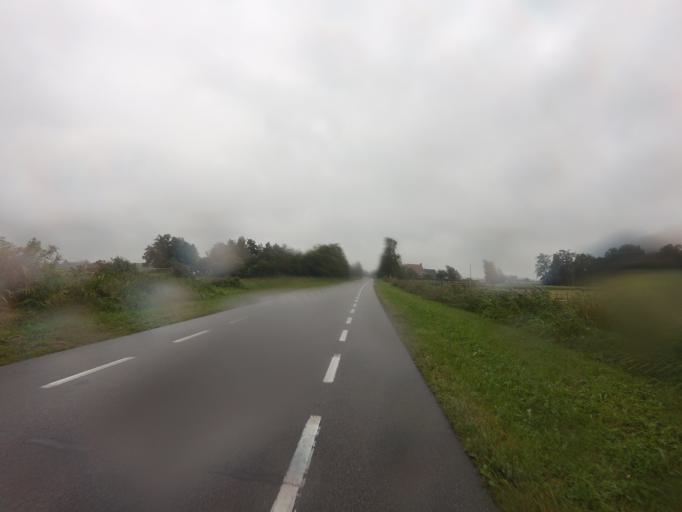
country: NL
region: Friesland
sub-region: Gemeente Smallingerland
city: Oudega
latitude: 53.0964
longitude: 5.9722
